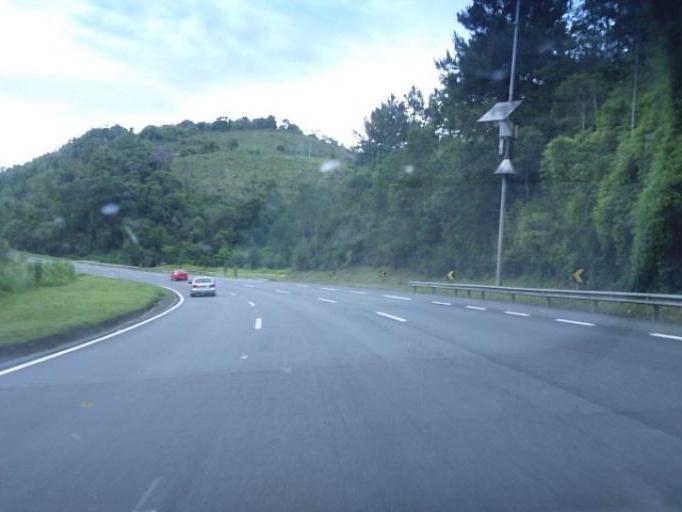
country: BR
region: Sao Paulo
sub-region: Cajati
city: Cajati
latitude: -24.9748
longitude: -48.5050
